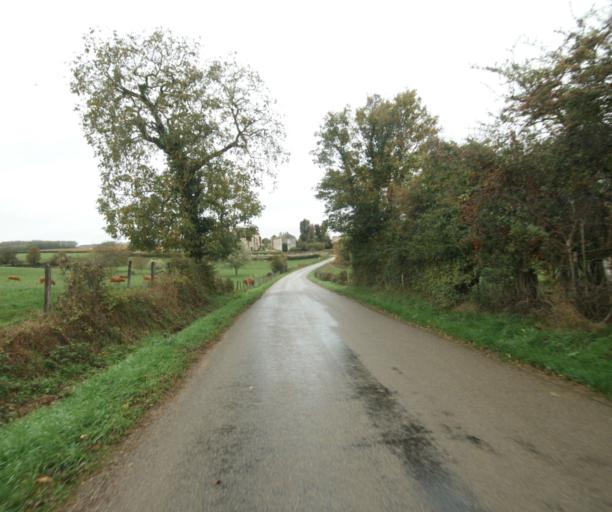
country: FR
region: Rhone-Alpes
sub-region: Departement de l'Ain
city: Pont-de-Vaux
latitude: 46.4822
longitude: 4.8623
